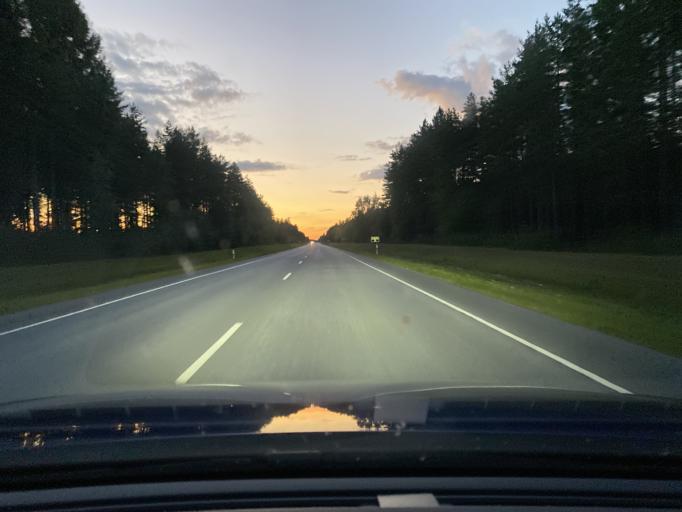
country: FI
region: Varsinais-Suomi
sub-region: Loimaa
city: Oripaeae
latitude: 60.9002
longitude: 22.6994
